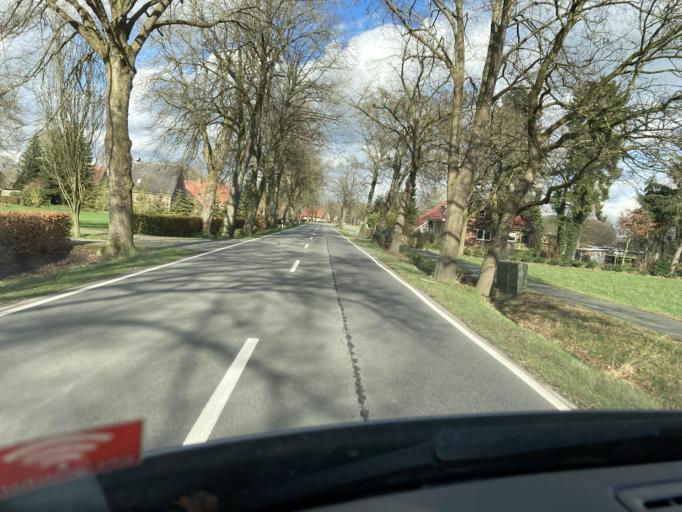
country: DE
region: Lower Saxony
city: Friedeburg
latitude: 53.3595
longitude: 7.8143
